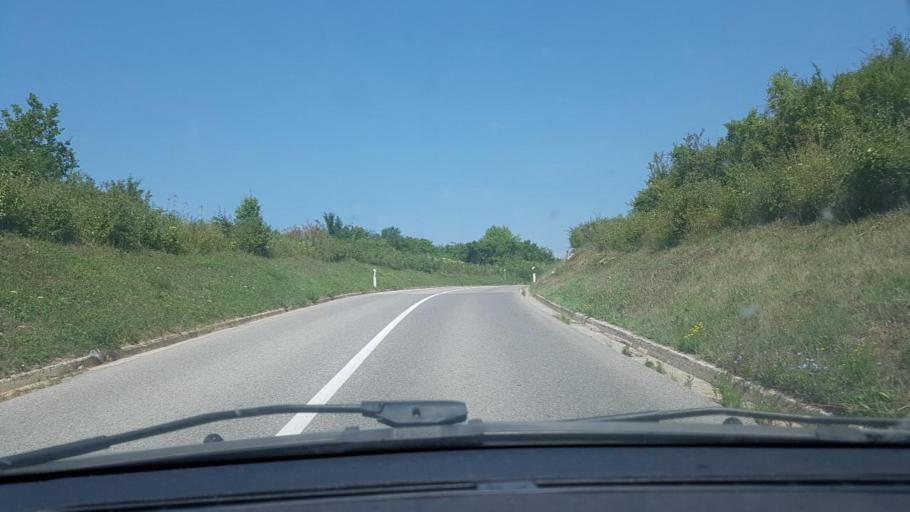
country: BA
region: Federation of Bosnia and Herzegovina
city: Velika Kladusa
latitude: 45.2054
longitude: 15.7727
